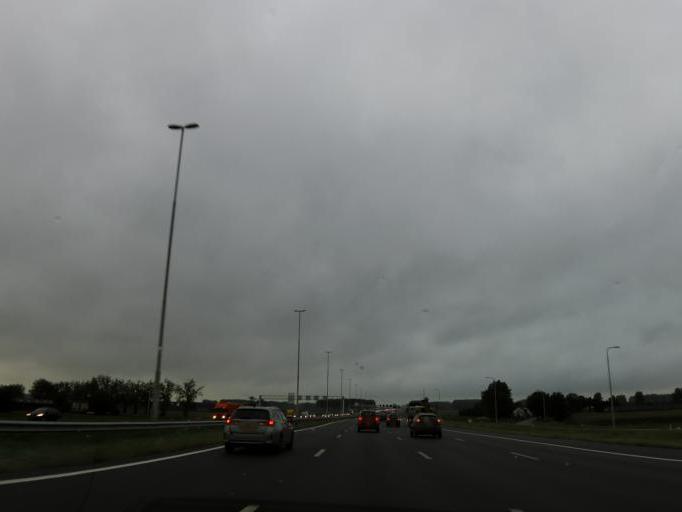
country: NL
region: Gelderland
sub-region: Gemeente Culemborg
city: Culemborg
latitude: 51.9014
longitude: 5.1881
